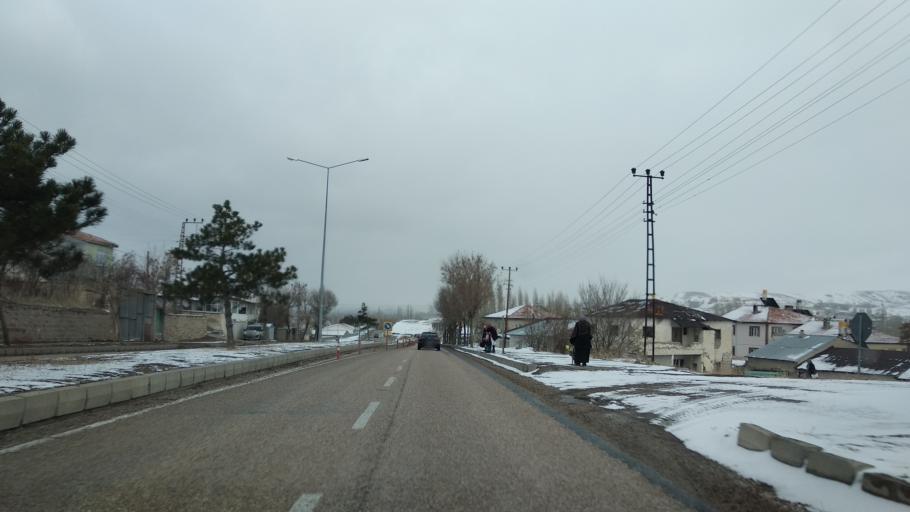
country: TR
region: Kayseri
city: Pinarbasi
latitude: 38.7258
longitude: 36.3956
